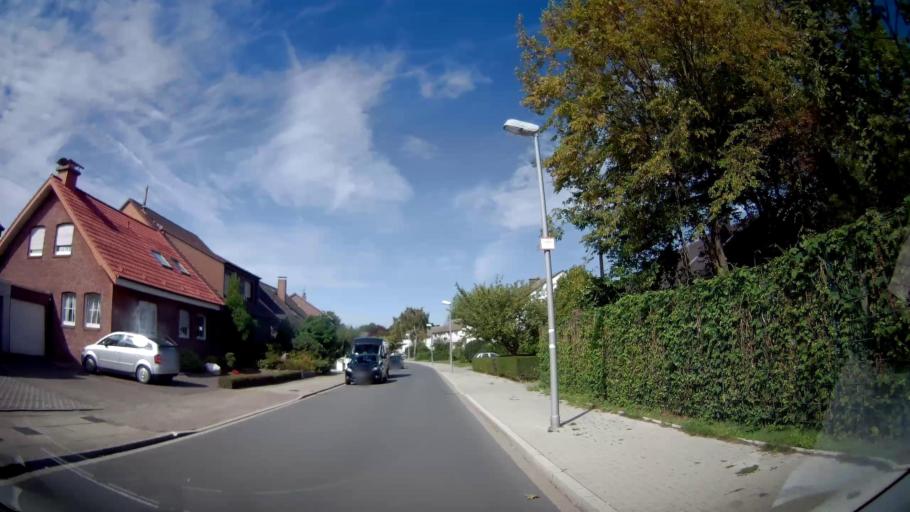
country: DE
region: North Rhine-Westphalia
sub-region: Regierungsbezirk Munster
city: Gladbeck
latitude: 51.5500
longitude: 7.0296
